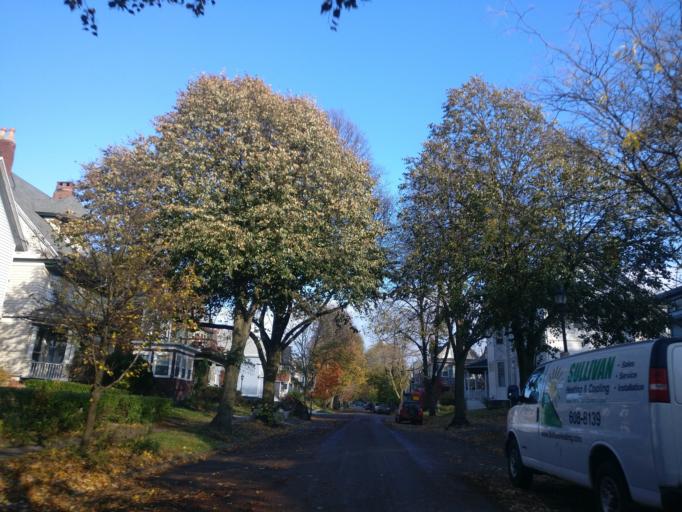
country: US
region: New York
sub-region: Erie County
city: Buffalo
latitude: 42.9123
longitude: -78.8812
